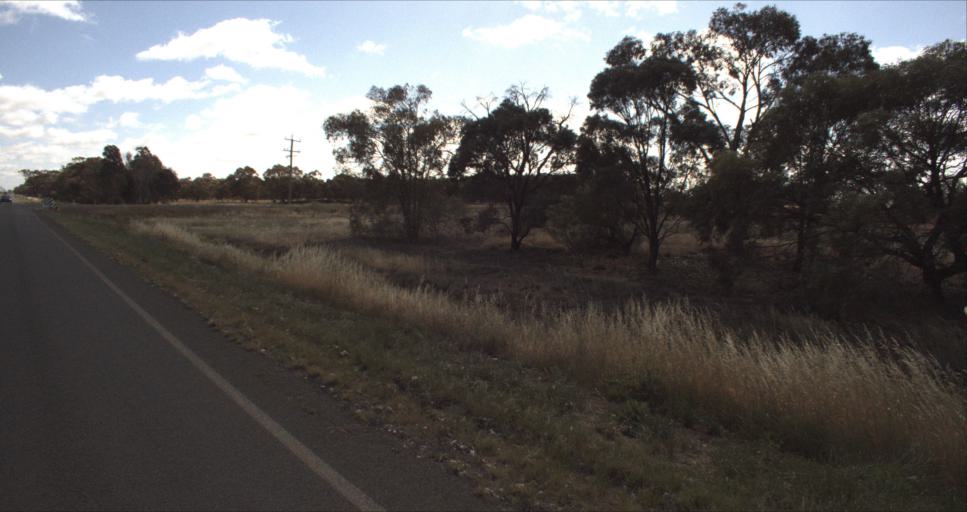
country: AU
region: New South Wales
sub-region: Murrumbidgee Shire
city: Darlington Point
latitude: -34.5422
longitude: 146.1719
